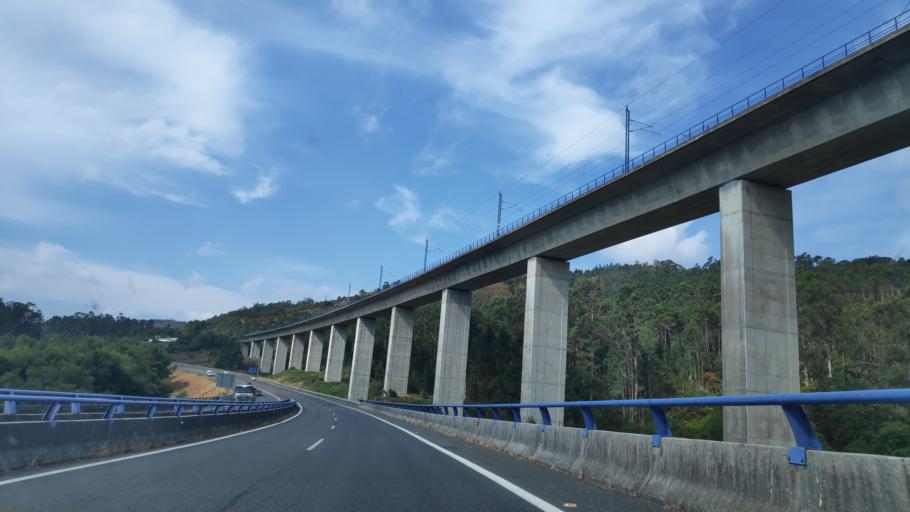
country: ES
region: Galicia
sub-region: Provincia da Coruna
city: Rois
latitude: 42.7273
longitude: -8.7174
